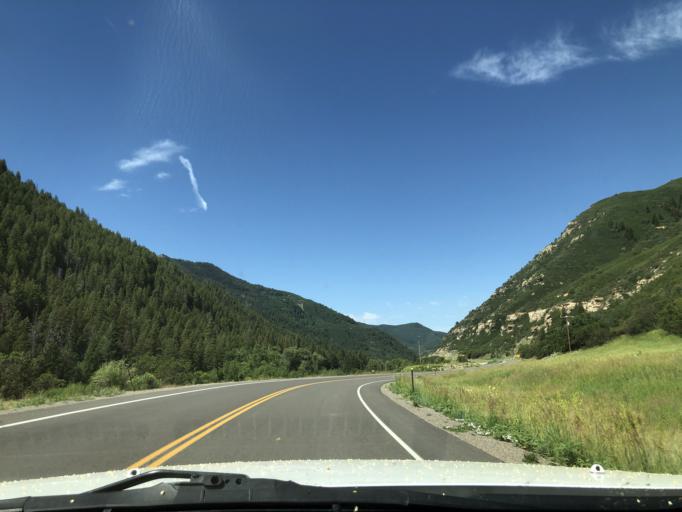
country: US
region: Colorado
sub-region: Delta County
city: Paonia
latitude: 38.9378
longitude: -107.3831
